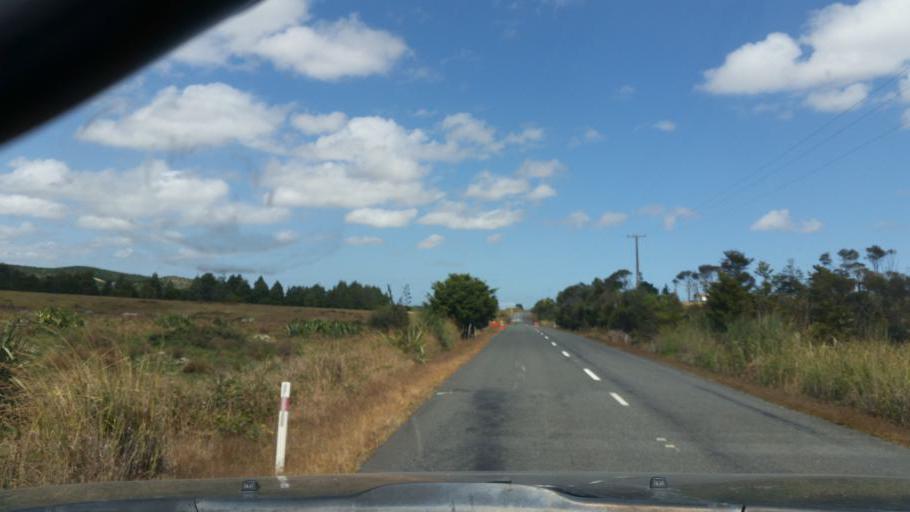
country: NZ
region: Northland
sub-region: Kaipara District
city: Dargaville
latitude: -35.8772
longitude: 173.8461
